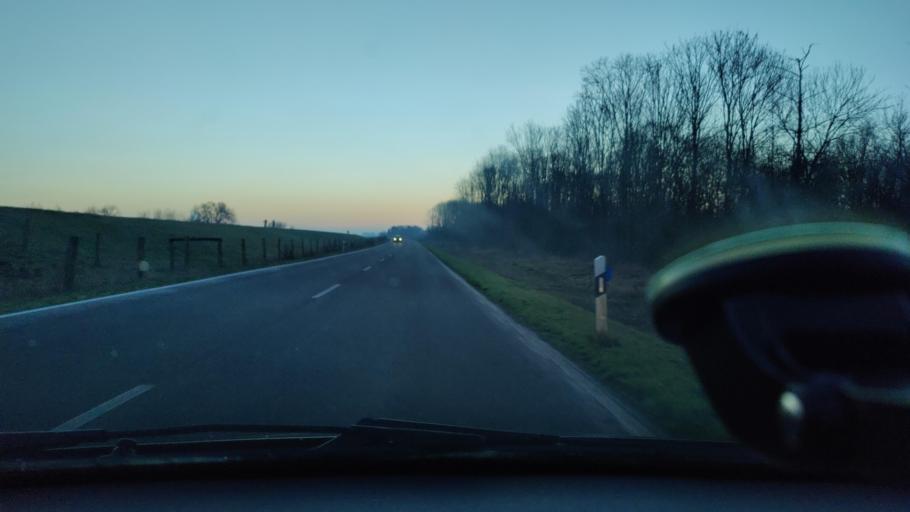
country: DE
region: North Rhine-Westphalia
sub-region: Regierungsbezirk Dusseldorf
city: Voerde
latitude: 51.5781
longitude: 6.6431
